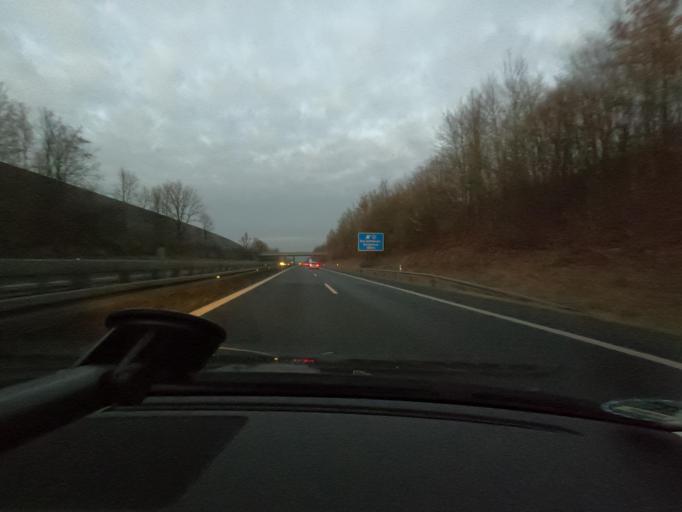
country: DE
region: Bavaria
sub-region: Upper Franconia
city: Bad Staffelstein
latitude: 50.0984
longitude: 11.0077
